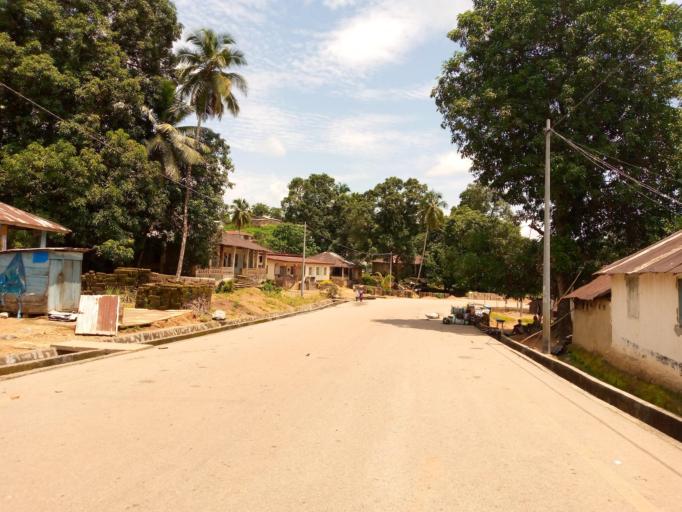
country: SL
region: Northern Province
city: Magburaka
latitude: 8.7249
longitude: -11.9519
